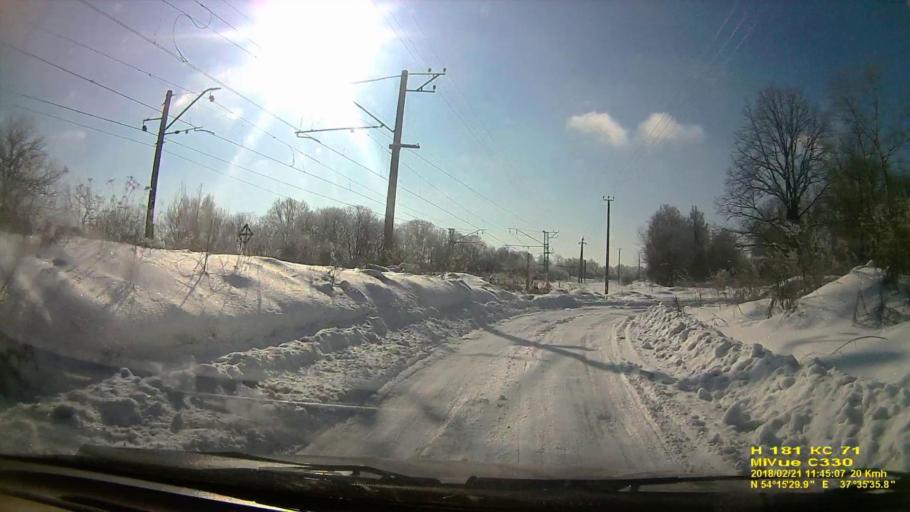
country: RU
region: Tula
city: Gorelki
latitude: 54.2583
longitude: 37.5933
